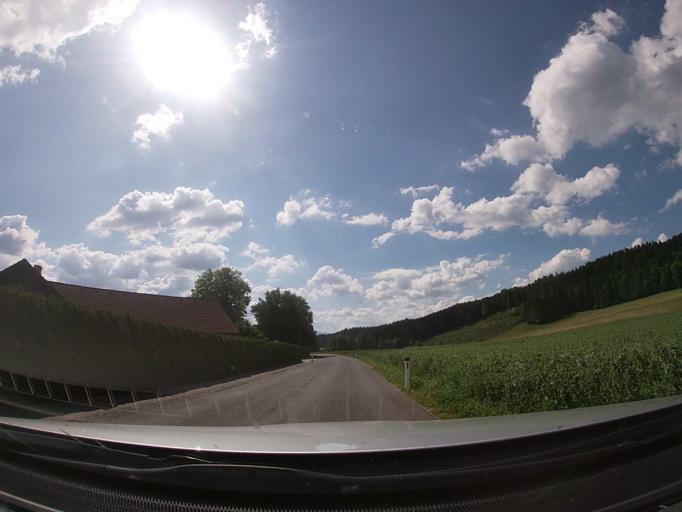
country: AT
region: Styria
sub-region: Politischer Bezirk Leoben
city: Trofaiach
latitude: 47.4281
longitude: 14.9795
